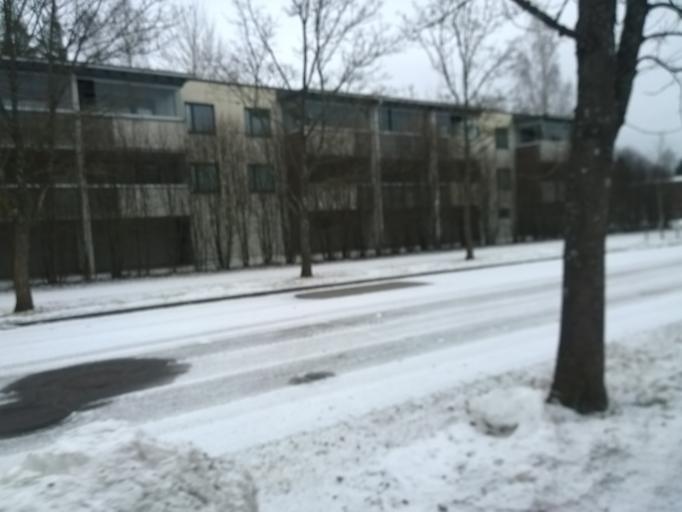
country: FI
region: Pirkanmaa
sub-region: Tampere
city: Tampere
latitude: 61.4439
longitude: 23.8424
